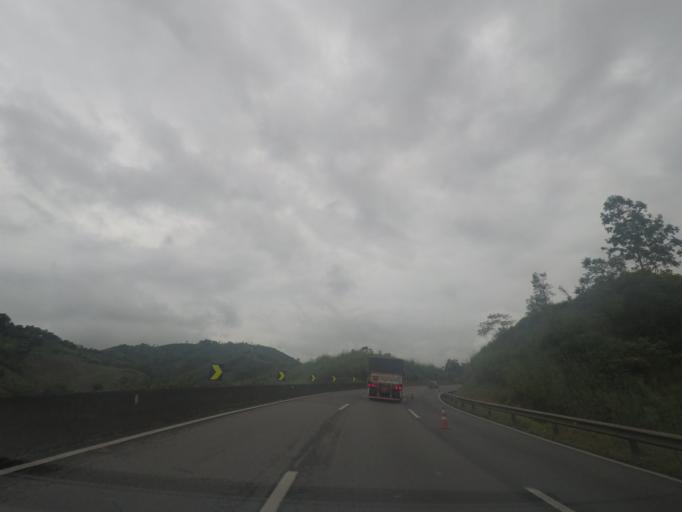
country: BR
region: Sao Paulo
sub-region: Cajati
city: Cajati
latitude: -24.7922
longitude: -48.2104
